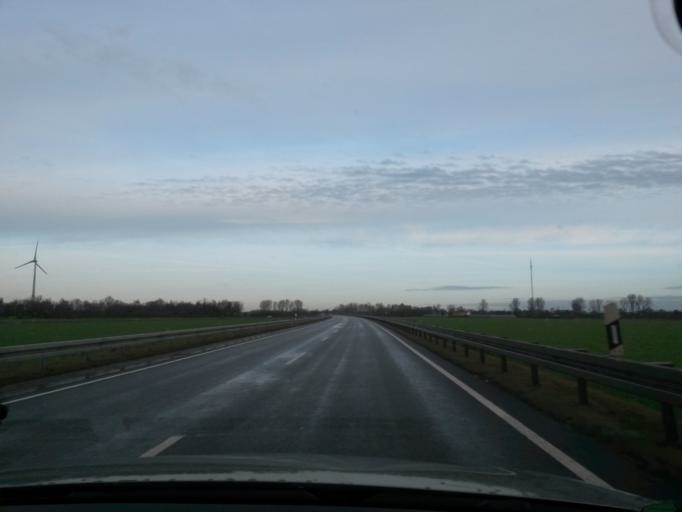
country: DE
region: North Rhine-Westphalia
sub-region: Regierungsbezirk Dusseldorf
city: Alpen
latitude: 51.6217
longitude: 6.5632
